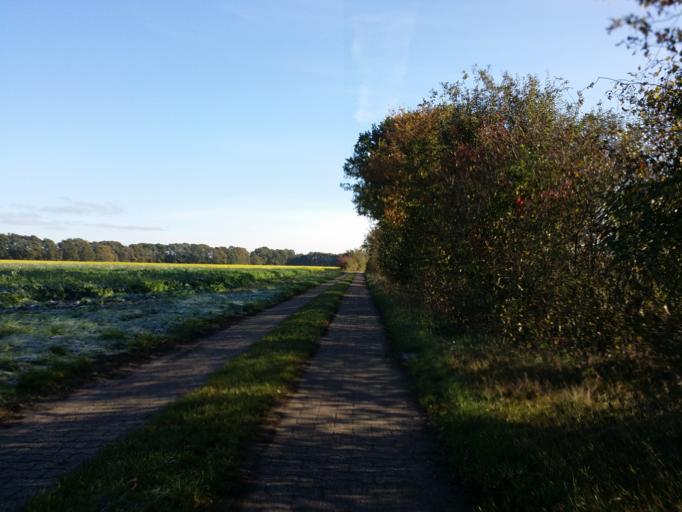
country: DE
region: Lower Saxony
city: Tarmstedt
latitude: 53.2033
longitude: 9.0675
